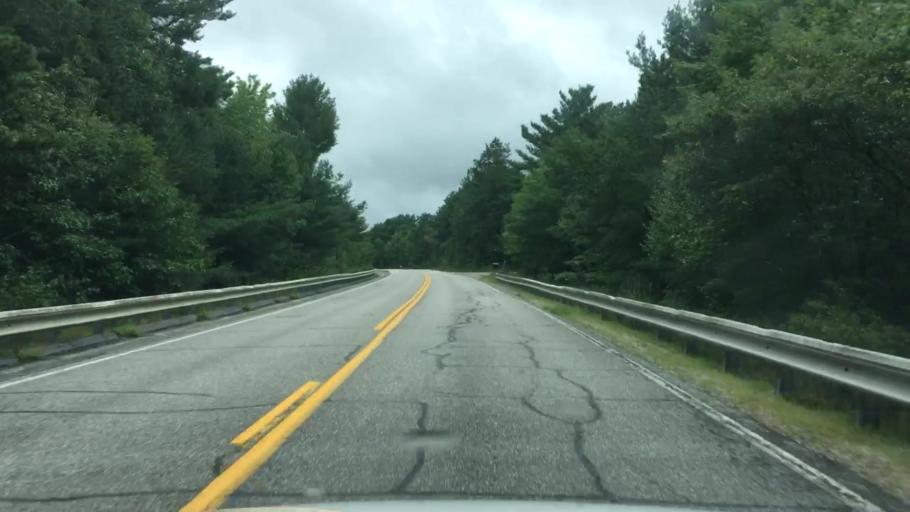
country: US
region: Maine
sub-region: Oxford County
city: Hiram
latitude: 43.9068
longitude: -70.8462
